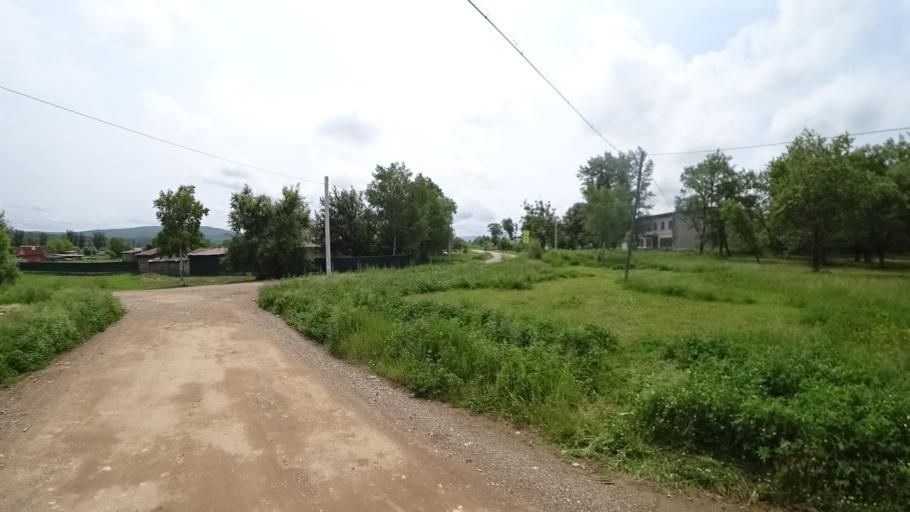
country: RU
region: Primorskiy
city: Novosysoyevka
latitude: 44.2400
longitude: 133.3639
